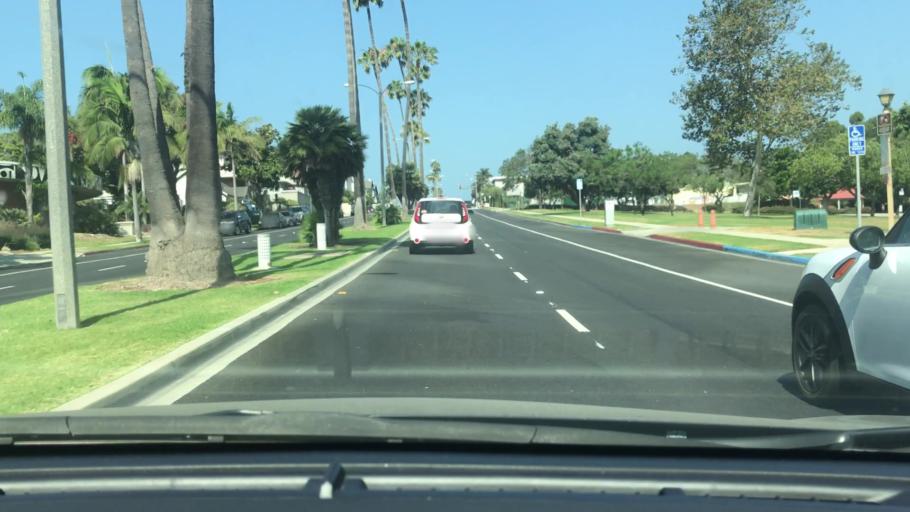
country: US
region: California
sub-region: Los Angeles County
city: Manhattan Beach
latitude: 33.8874
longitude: -118.3848
